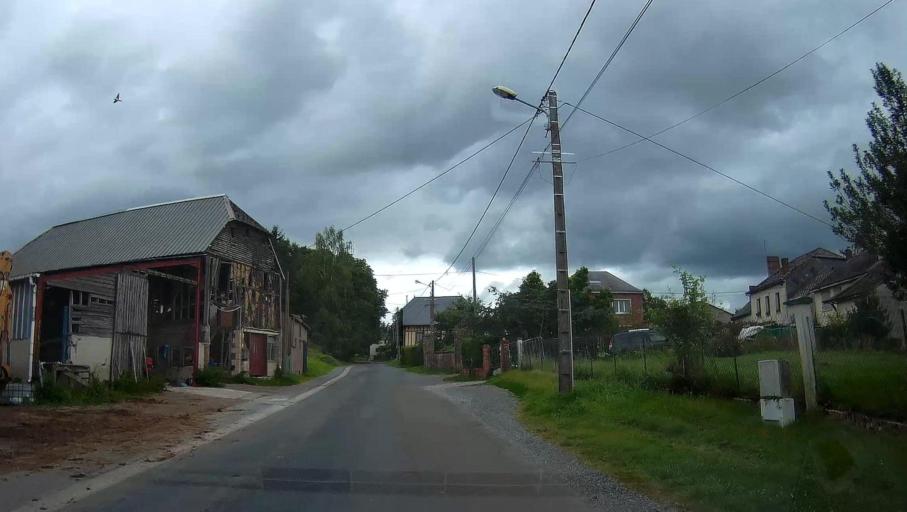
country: FR
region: Picardie
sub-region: Departement de l'Aisne
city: Rozoy-sur-Serre
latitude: 49.6913
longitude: 4.2463
